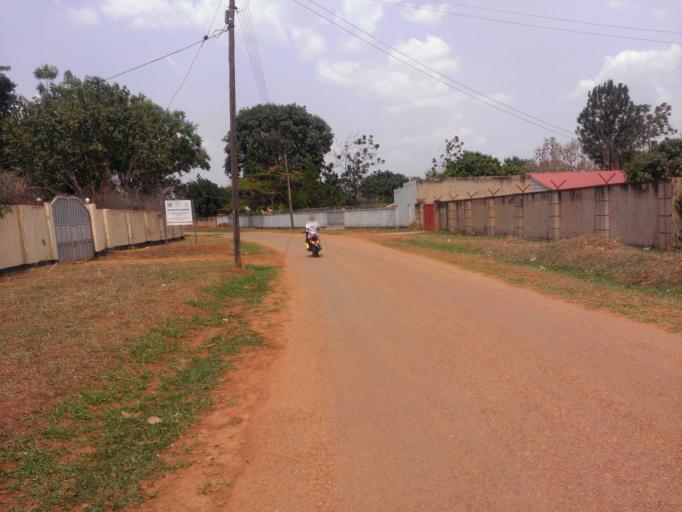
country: UG
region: Northern Region
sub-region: Gulu District
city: Gulu
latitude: 2.7823
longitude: 32.3037
